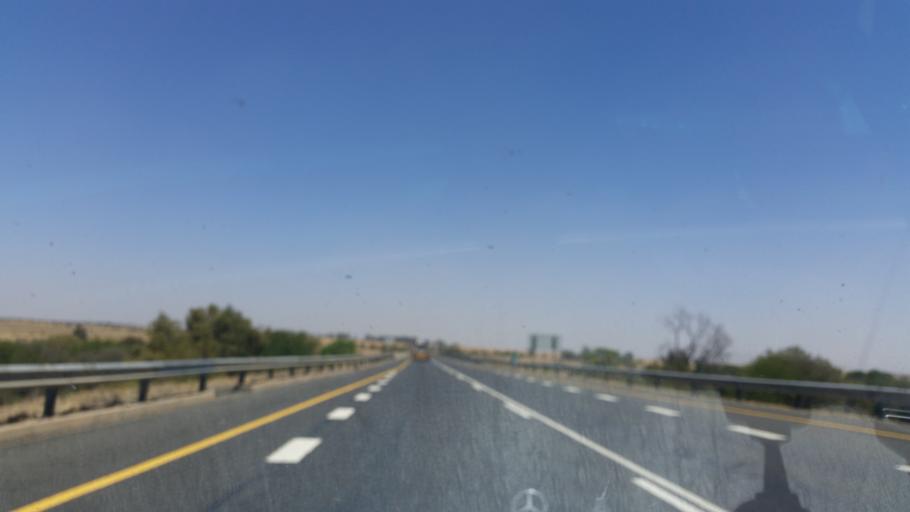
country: ZA
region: Orange Free State
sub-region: Lejweleputswa District Municipality
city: Winburg
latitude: -28.6305
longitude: 26.9053
